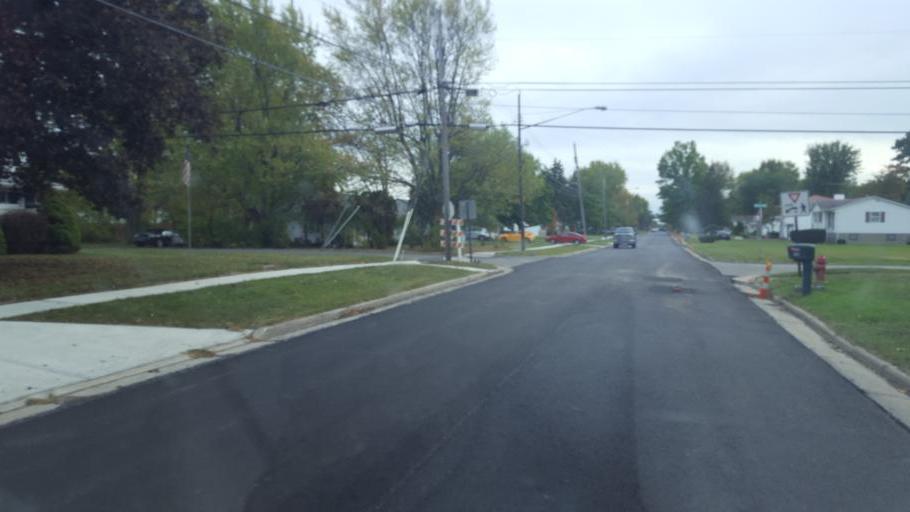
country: US
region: Ohio
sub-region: Lorain County
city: Sheffield Lake
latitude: 41.4829
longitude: -82.1133
